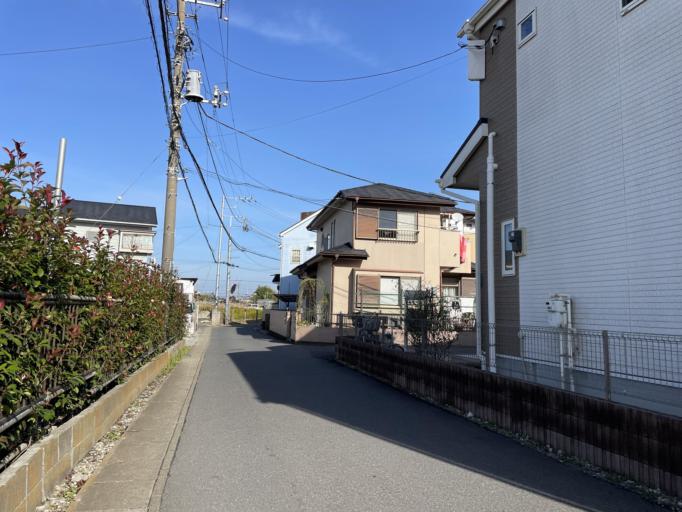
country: JP
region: Chiba
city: Kashiwa
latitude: 35.7793
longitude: 139.9891
